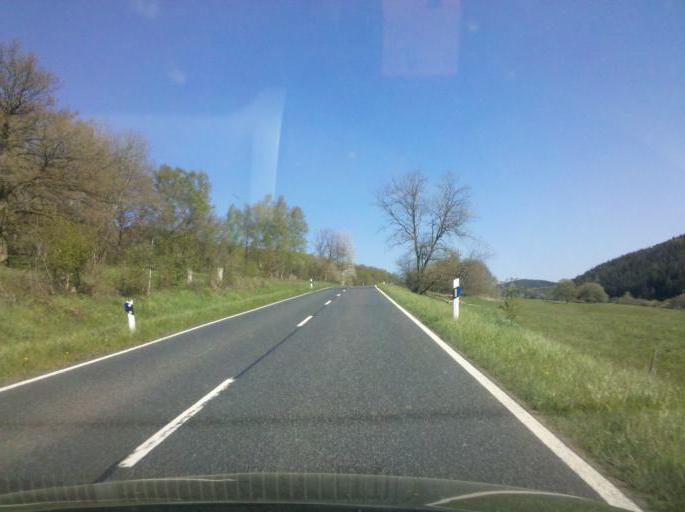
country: DE
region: Hesse
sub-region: Regierungsbezirk Giessen
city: Haiger
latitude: 50.7698
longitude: 8.1891
